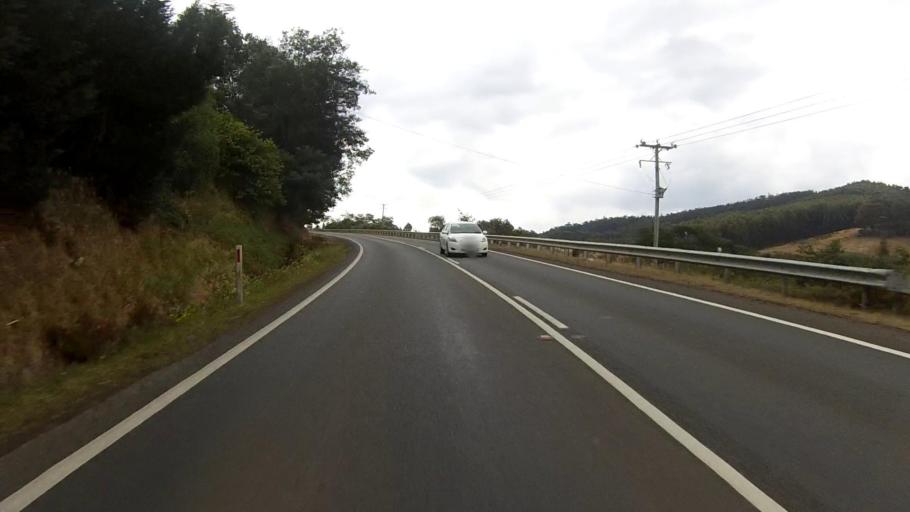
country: AU
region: Tasmania
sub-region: Huon Valley
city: Cygnet
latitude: -43.1353
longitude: 147.0538
